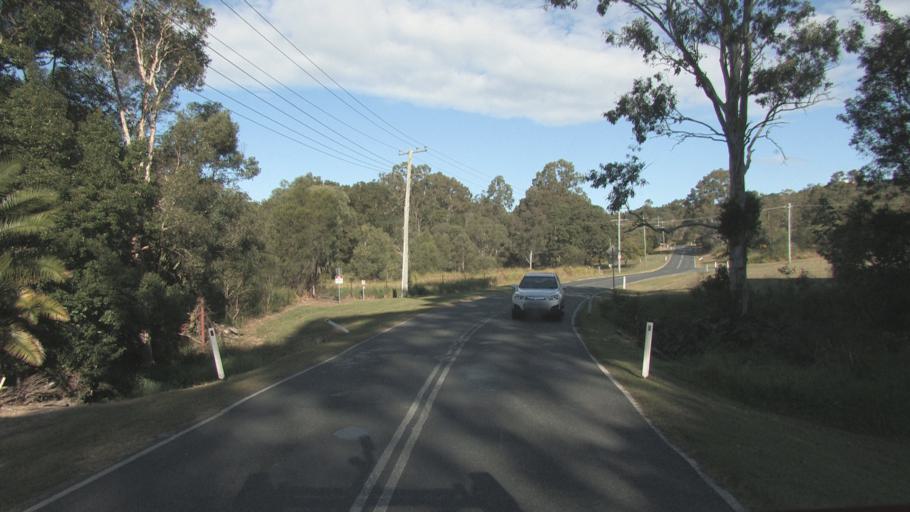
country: AU
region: Queensland
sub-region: Logan
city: Windaroo
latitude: -27.7331
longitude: 153.1718
